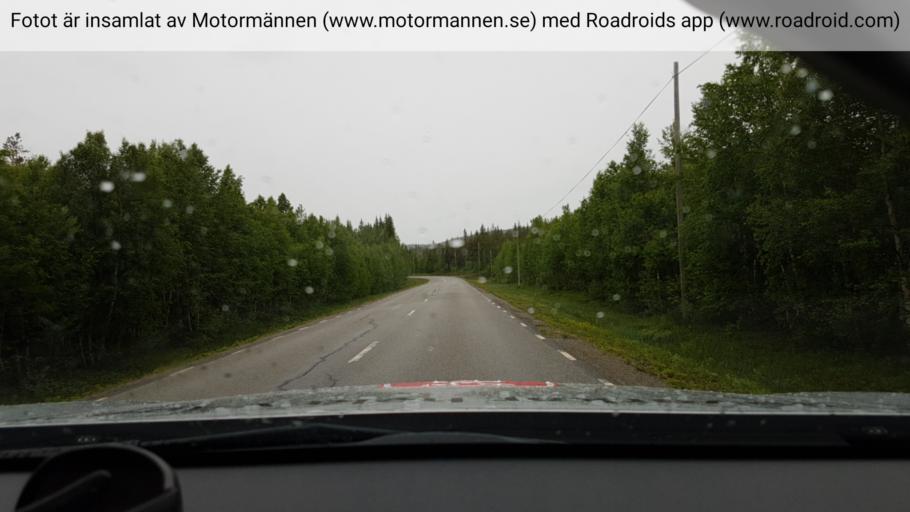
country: SE
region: Vaesterbotten
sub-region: Storumans Kommun
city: Fristad
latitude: 65.8354
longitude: 16.6121
